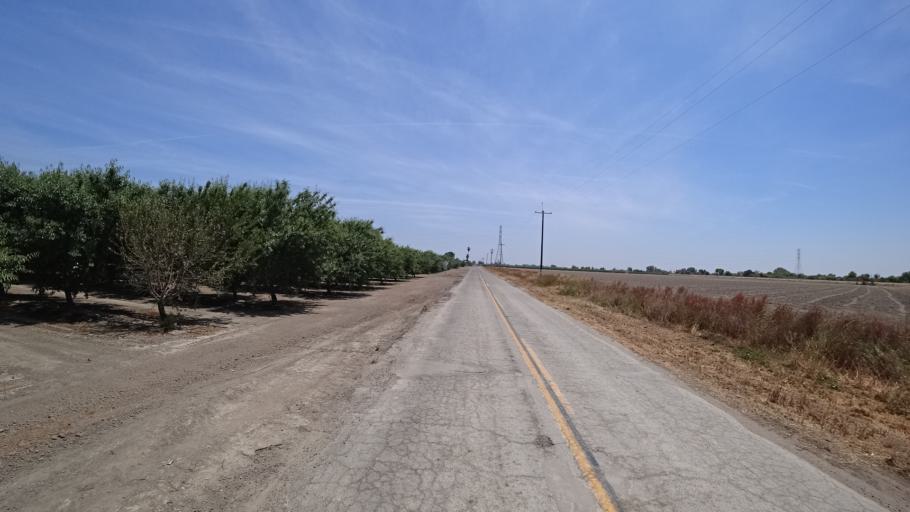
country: US
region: California
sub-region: Fresno County
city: Riverdale
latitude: 36.3875
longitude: -119.8950
